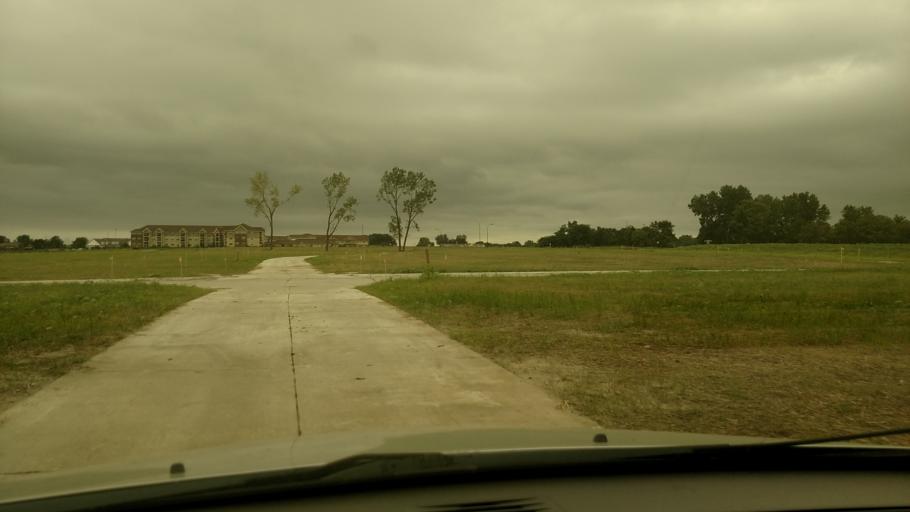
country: US
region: Iowa
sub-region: Polk County
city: Ankeny
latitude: 41.7141
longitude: -93.6128
